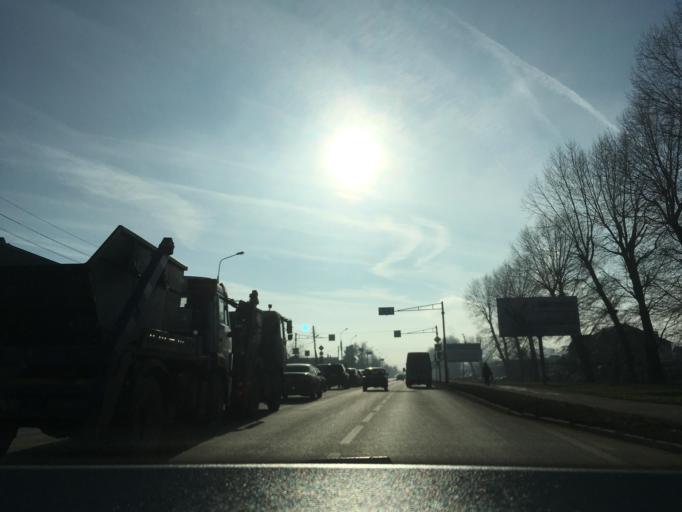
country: RU
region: Krasnodarskiy
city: Krasnodar
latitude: 45.1051
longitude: 39.0127
